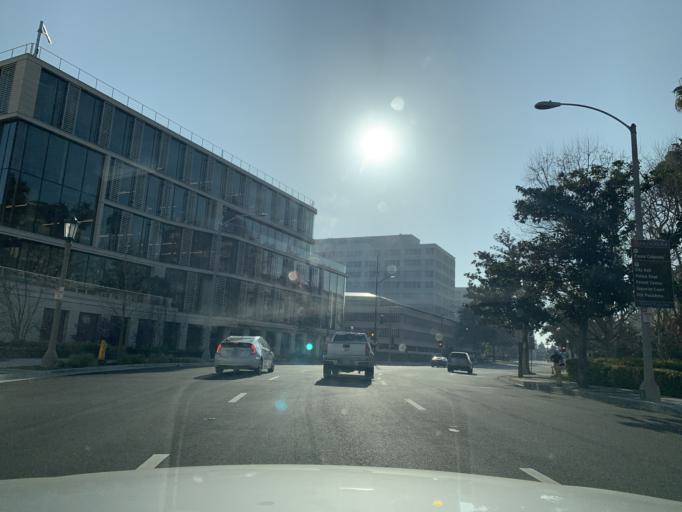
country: US
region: California
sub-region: Los Angeles County
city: Pasadena
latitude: 34.1471
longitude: -118.1421
